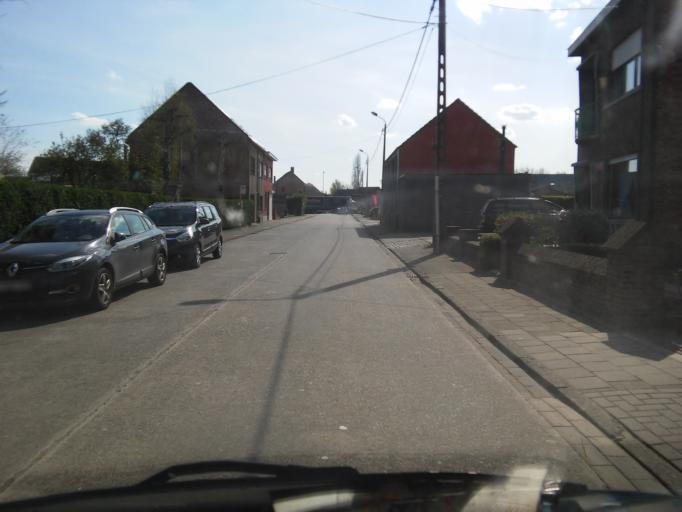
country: BE
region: Flanders
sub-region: Provincie Antwerpen
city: Willebroek
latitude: 51.0484
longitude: 4.3806
